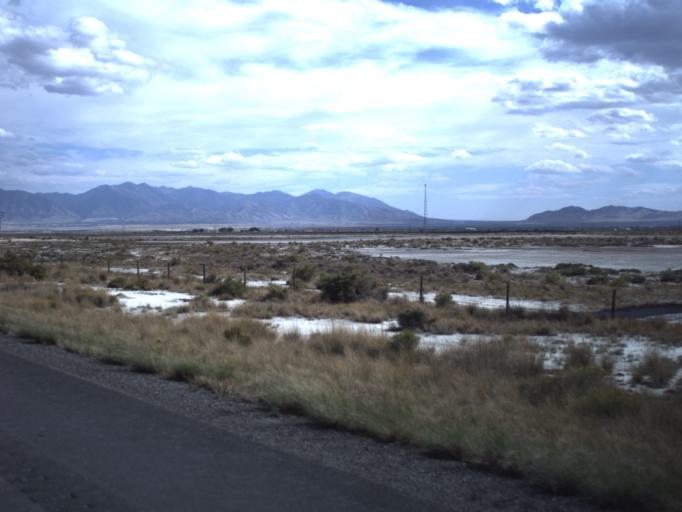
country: US
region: Utah
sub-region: Tooele County
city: Grantsville
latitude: 40.6900
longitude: -112.4610
